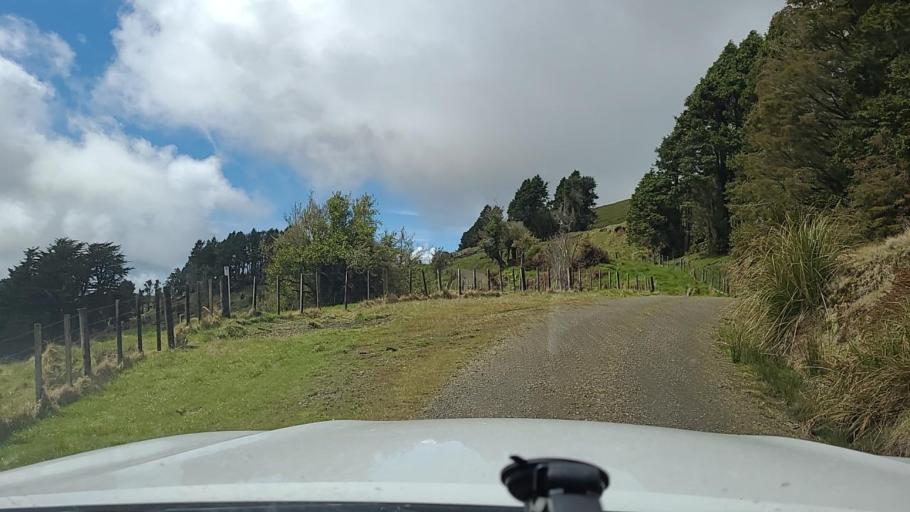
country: NZ
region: Bay of Plenty
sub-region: Opotiki District
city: Opotiki
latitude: -38.2874
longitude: 177.5794
